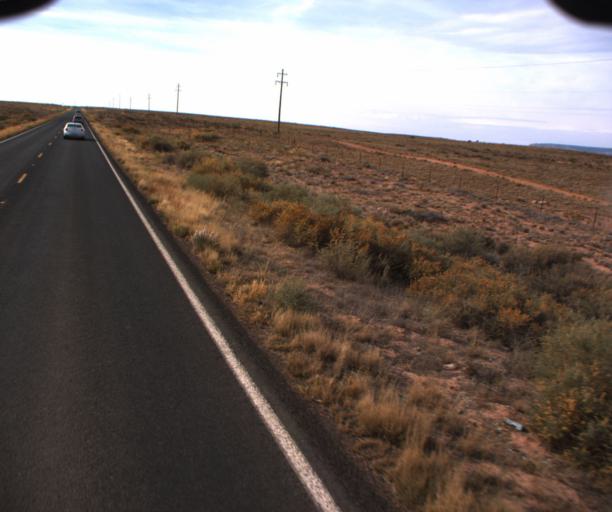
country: US
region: Arizona
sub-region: Apache County
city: Ganado
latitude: 35.9224
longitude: -109.6071
